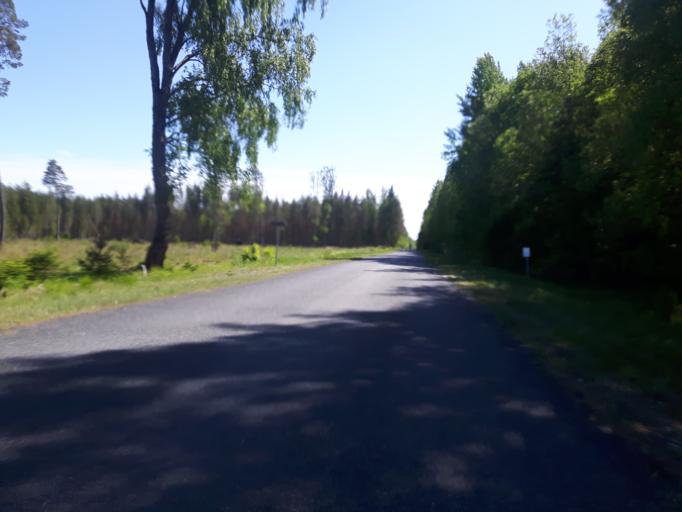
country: EE
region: Laeaene-Virumaa
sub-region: Haljala vald
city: Haljala
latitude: 59.5537
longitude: 26.2391
